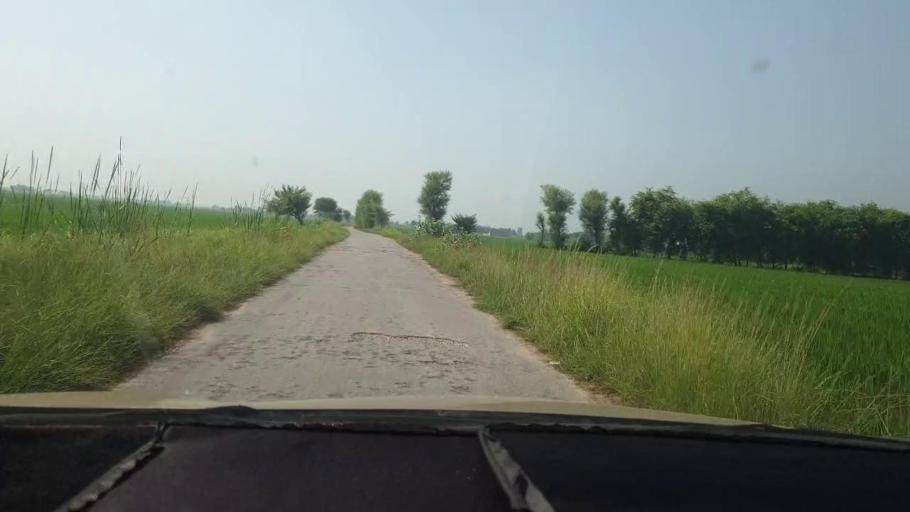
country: PK
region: Sindh
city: Kambar
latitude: 27.5808
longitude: 68.0553
